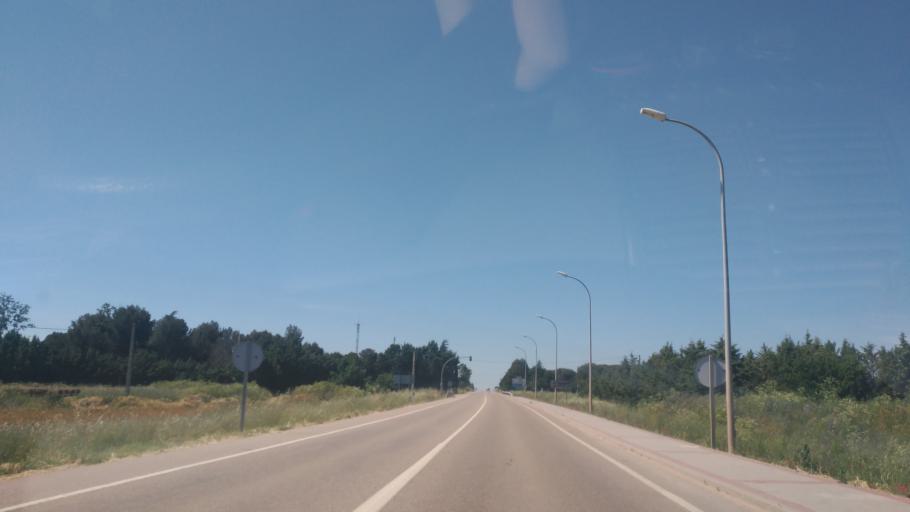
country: ES
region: Castille and Leon
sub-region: Provincia de Salamanca
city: Villares de la Reina
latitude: 41.0219
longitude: -5.6709
